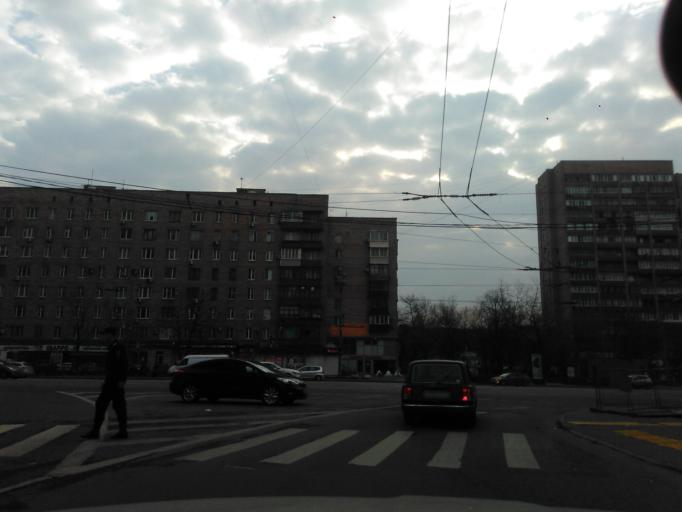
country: RU
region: Moscow
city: Mar'ina Roshcha
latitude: 55.7955
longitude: 37.5836
